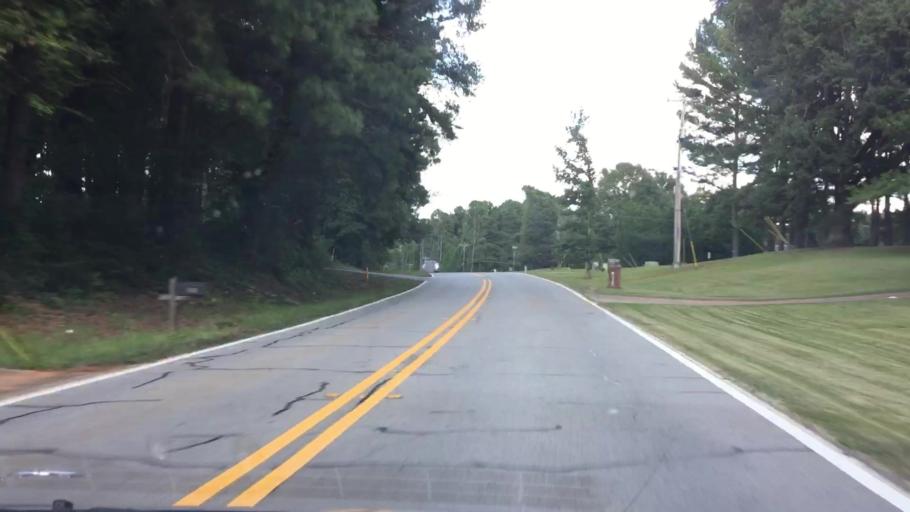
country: US
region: Georgia
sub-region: Fayette County
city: Shannon
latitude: 33.4141
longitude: -84.4814
